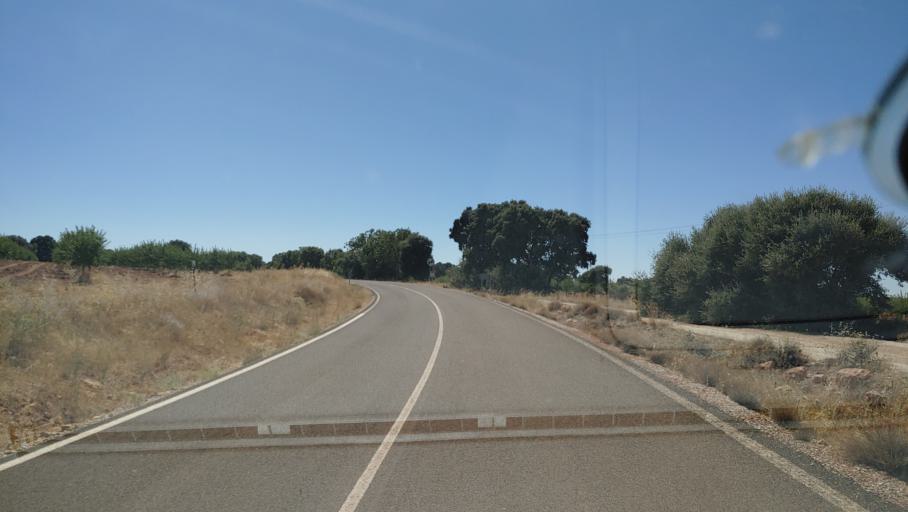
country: ES
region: Castille-La Mancha
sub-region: Provincia de Ciudad Real
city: Villahermosa
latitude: 38.8330
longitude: -2.8247
